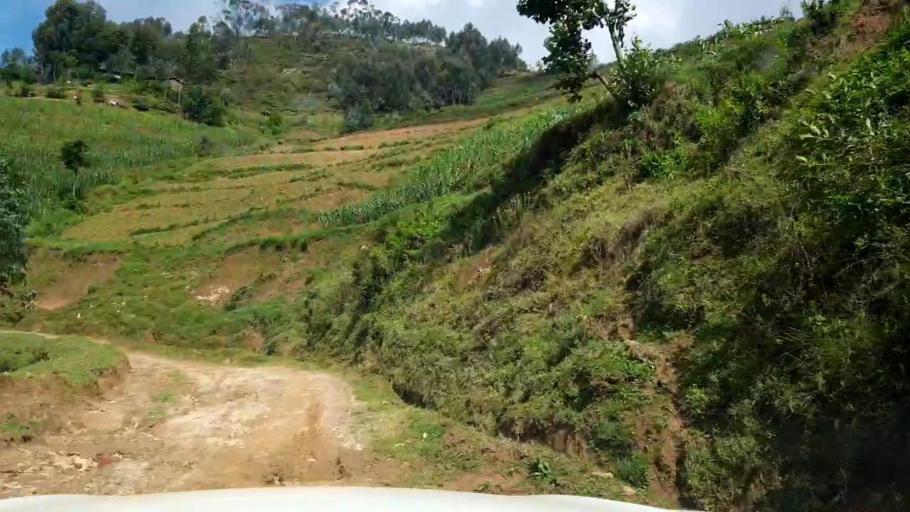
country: RW
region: Western Province
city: Kibuye
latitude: -1.8823
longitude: 29.4713
